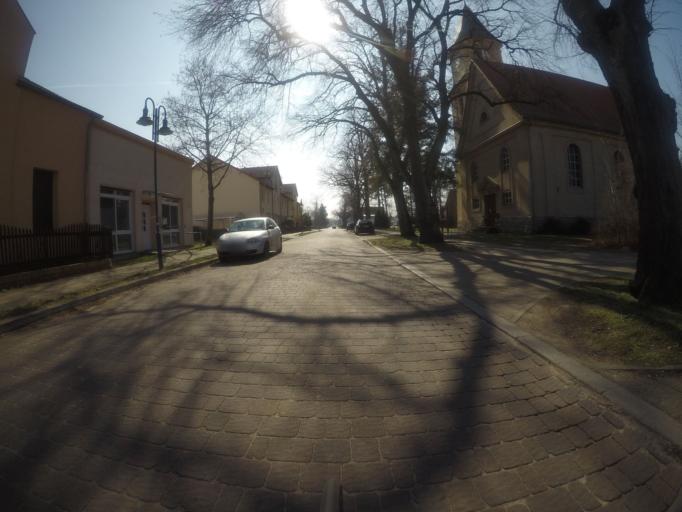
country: DE
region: Brandenburg
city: Erkner
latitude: 52.3943
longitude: 13.7127
